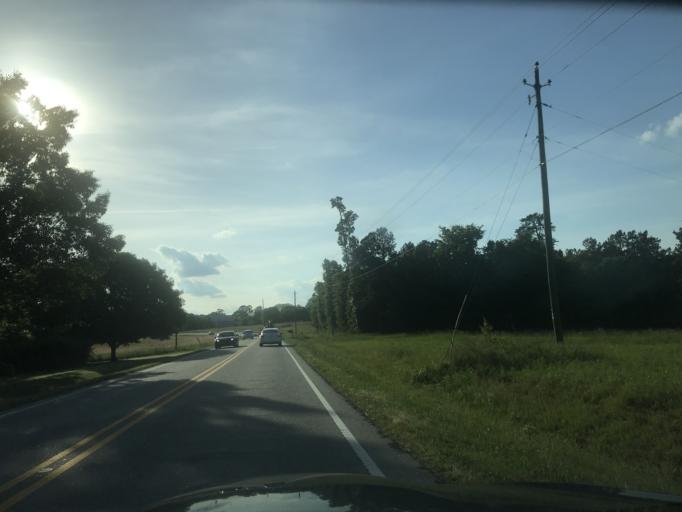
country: US
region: North Carolina
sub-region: Wake County
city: Knightdale
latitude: 35.7503
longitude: -78.4712
